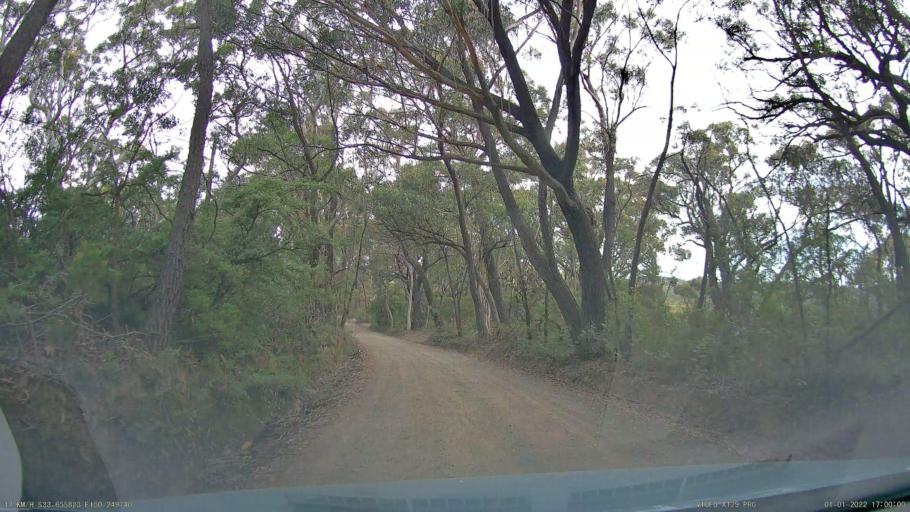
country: AU
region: New South Wales
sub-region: Blue Mountains Municipality
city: Blackheath
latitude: -33.6559
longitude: 150.2498
